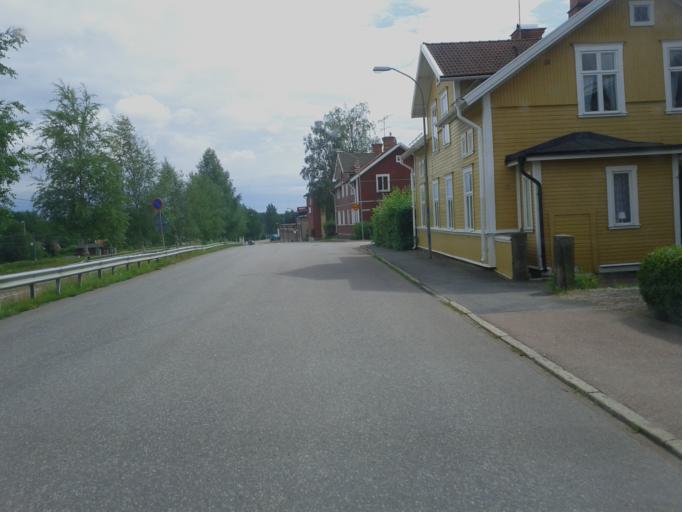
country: SE
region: Dalarna
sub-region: Saters Kommun
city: Saeter
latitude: 60.3457
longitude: 15.7576
